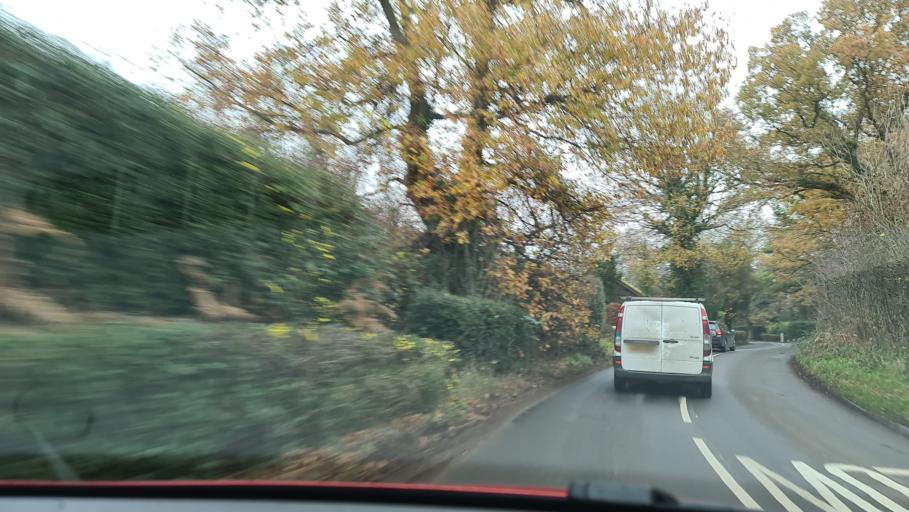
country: GB
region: England
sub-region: Buckinghamshire
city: Seer Green
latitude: 51.6135
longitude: -0.5929
